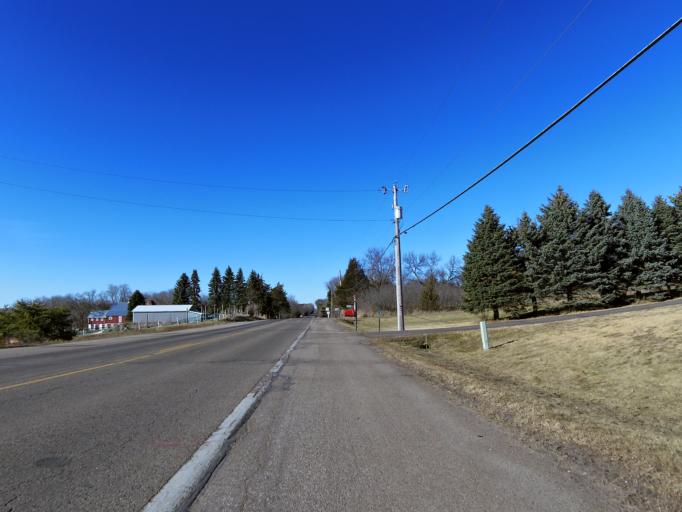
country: US
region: Minnesota
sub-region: Washington County
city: Oak Park Heights
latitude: 44.9906
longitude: -92.8223
